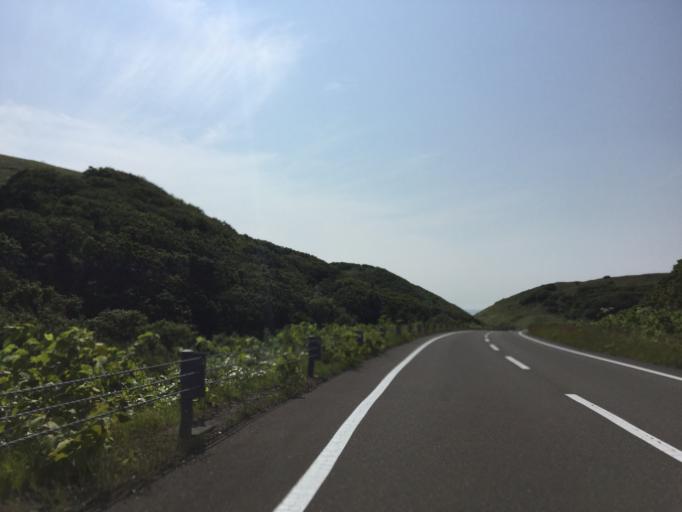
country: JP
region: Hokkaido
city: Makubetsu
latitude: 45.4970
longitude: 141.8927
